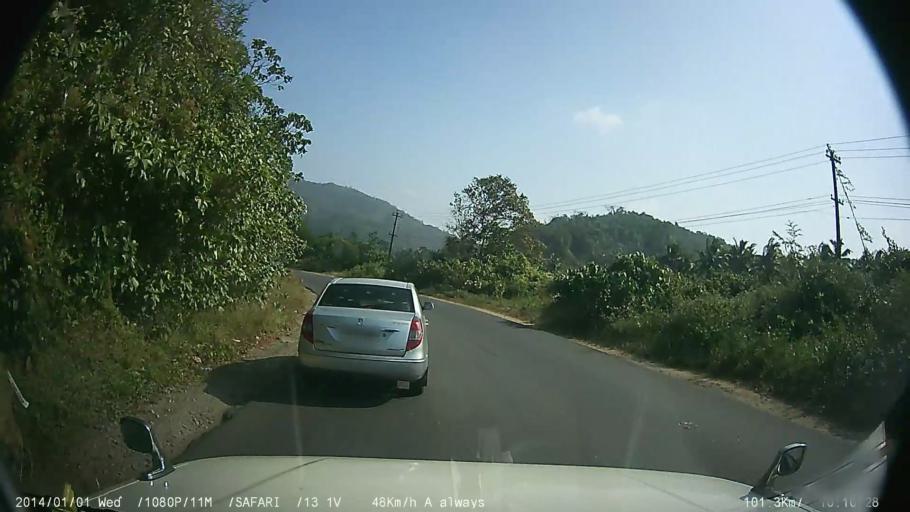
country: IN
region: Kerala
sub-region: Thrissur District
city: Chelakara
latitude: 10.5730
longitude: 76.3902
